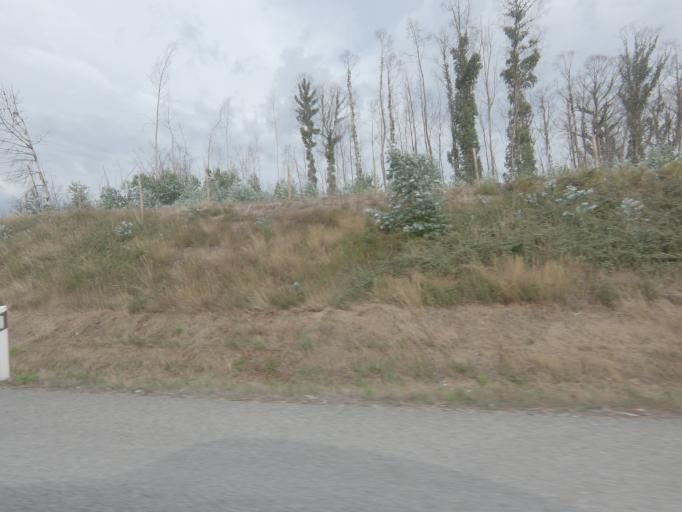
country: PT
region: Viseu
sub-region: Santa Comba Dao
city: Santa Comba Dao
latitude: 40.4521
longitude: -8.1052
